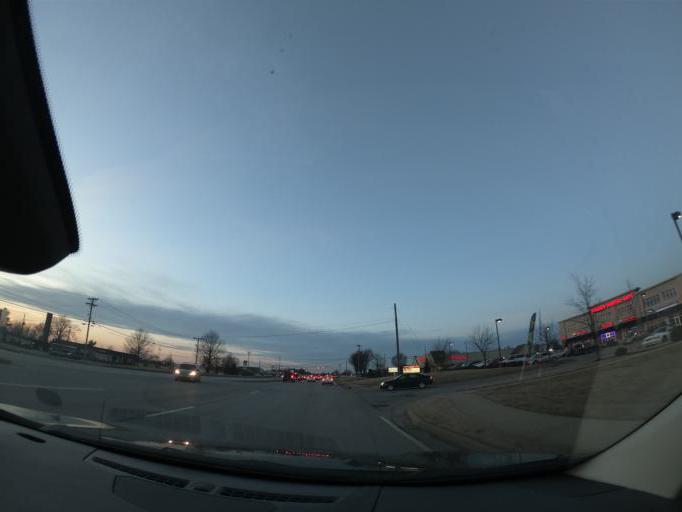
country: US
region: Kentucky
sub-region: Jefferson County
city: Worthington
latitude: 38.2863
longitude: -85.5710
